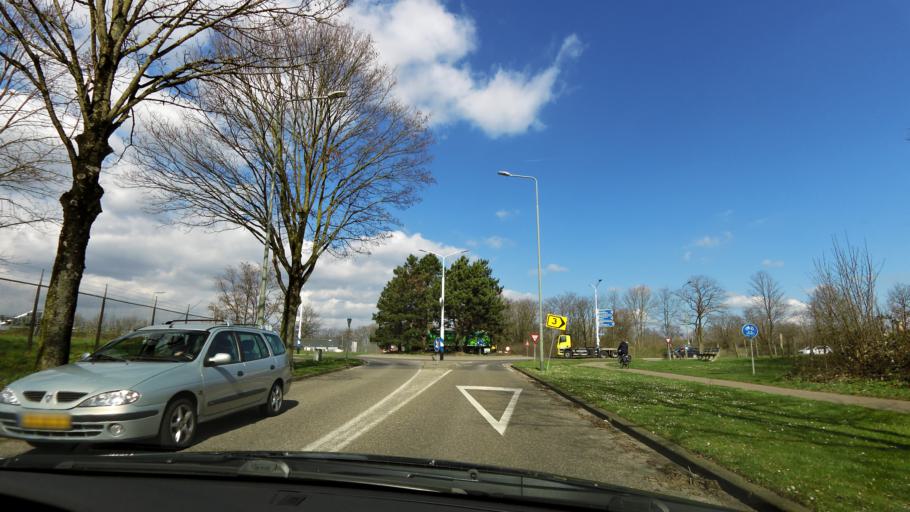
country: NL
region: Limburg
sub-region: Gemeente Stein
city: Urmond
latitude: 50.9812
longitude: 5.7688
